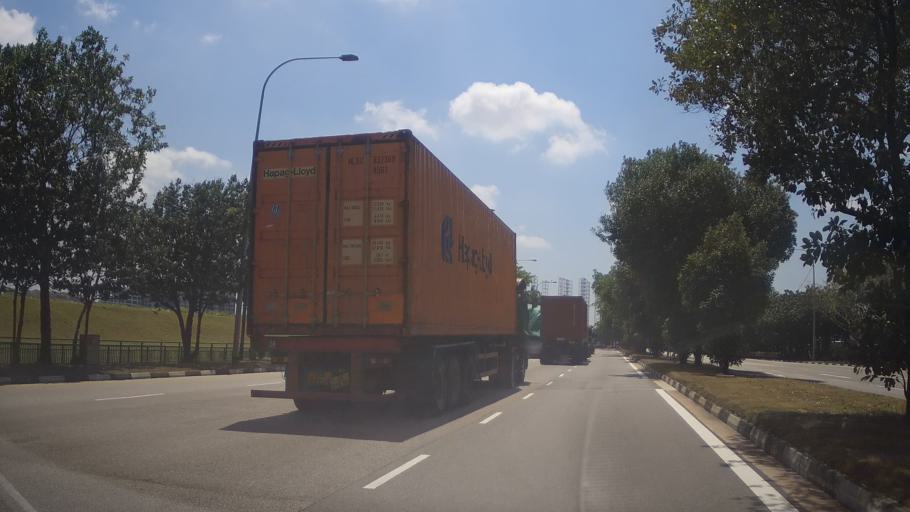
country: SG
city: Singapore
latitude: 1.3071
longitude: 103.7404
